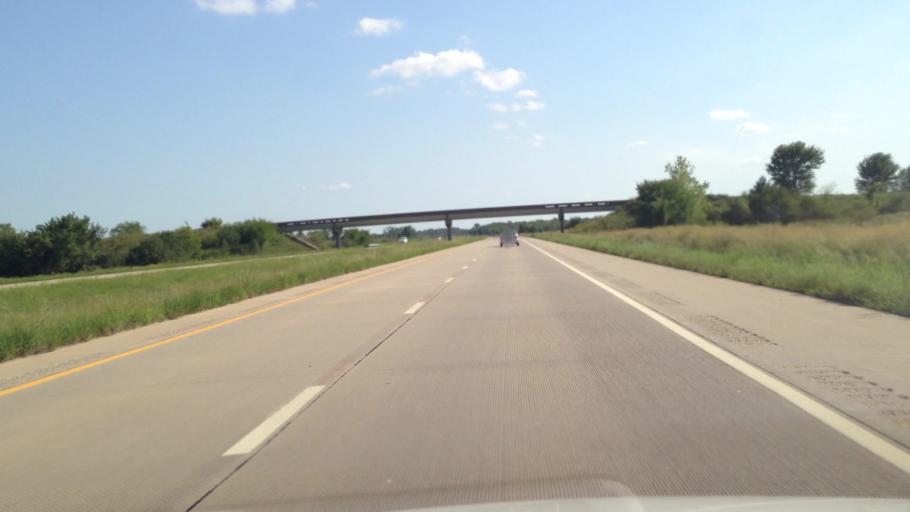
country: US
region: Kansas
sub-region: Bourbon County
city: Fort Scott
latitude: 37.9233
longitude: -94.7046
